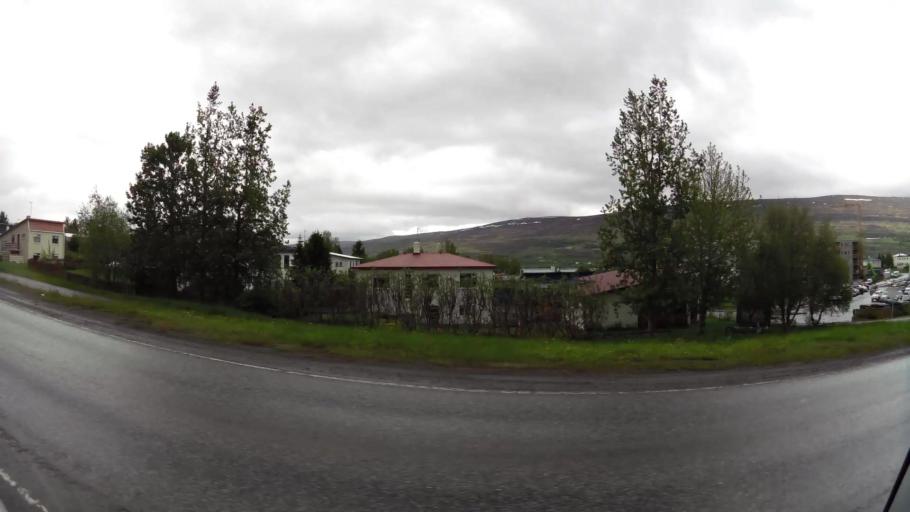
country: IS
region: Northeast
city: Akureyri
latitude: 65.6925
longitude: -18.1118
